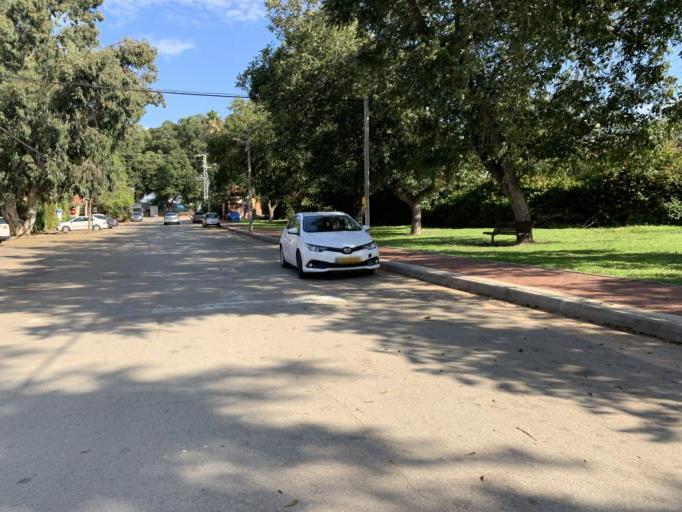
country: IL
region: Central District
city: Ra'anana
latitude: 32.1669
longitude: 34.8744
